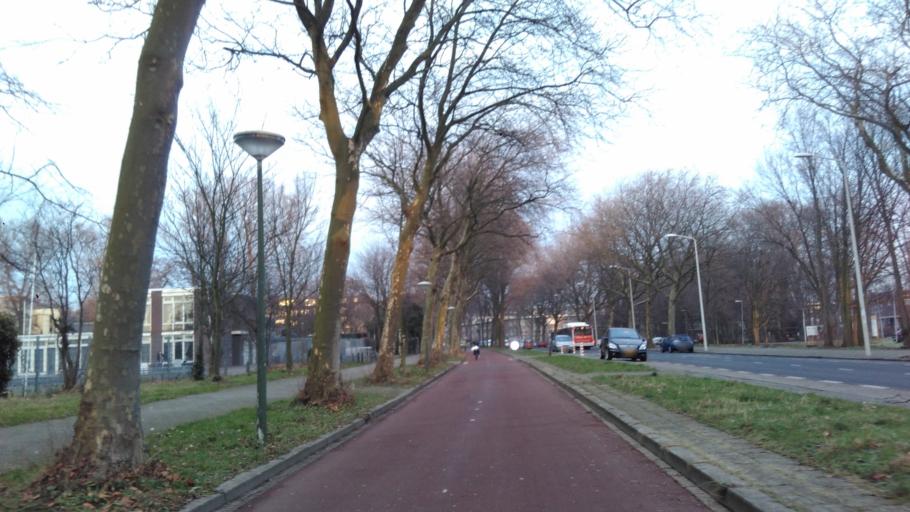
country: NL
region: South Holland
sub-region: Gemeente Westland
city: Poeldijk
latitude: 52.0623
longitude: 4.2493
